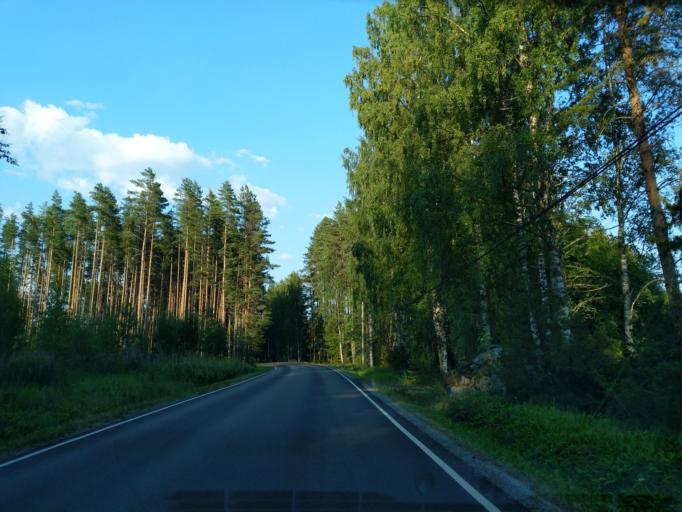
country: FI
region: Satakunta
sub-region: Pohjois-Satakunta
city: Honkajoki
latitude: 61.8197
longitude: 22.2252
